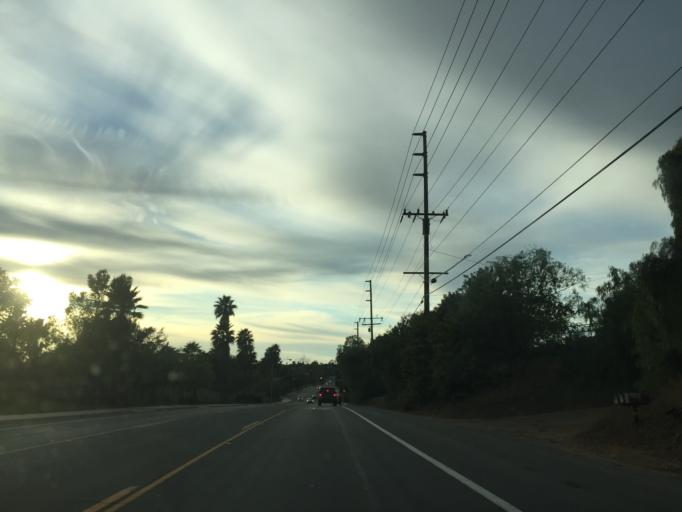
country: US
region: California
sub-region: Santa Barbara County
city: Goleta
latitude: 34.4515
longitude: -119.7943
